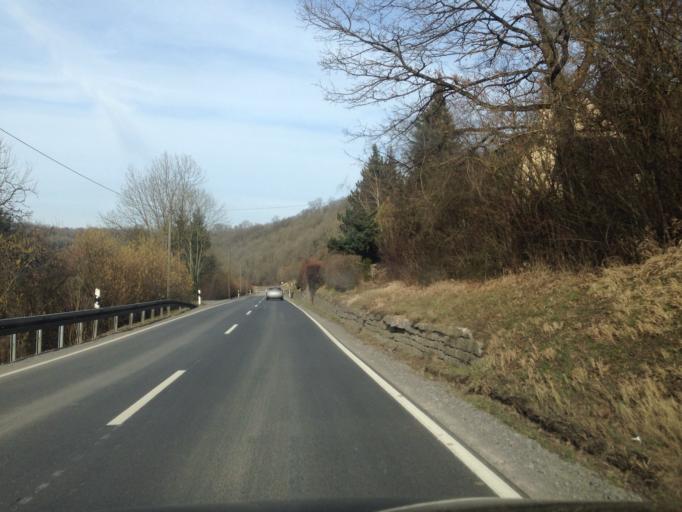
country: DE
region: Baden-Wuerttemberg
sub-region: Regierungsbezirk Stuttgart
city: Widdern
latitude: 49.3155
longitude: 9.4299
